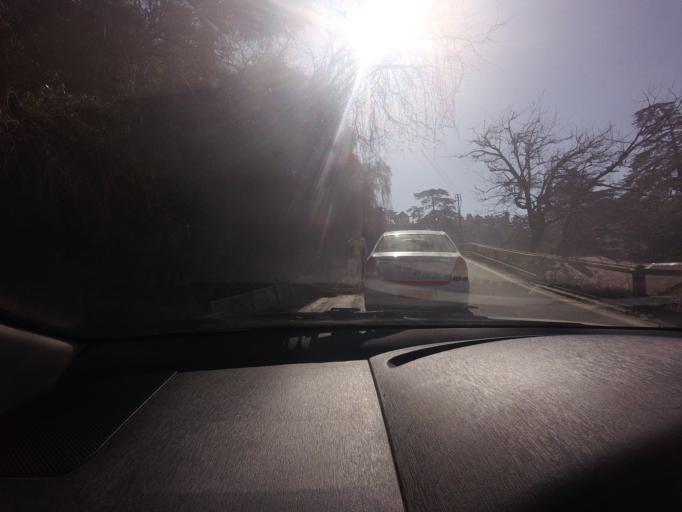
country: IN
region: Himachal Pradesh
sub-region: Shimla
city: Shimla
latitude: 31.1079
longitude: 77.1653
